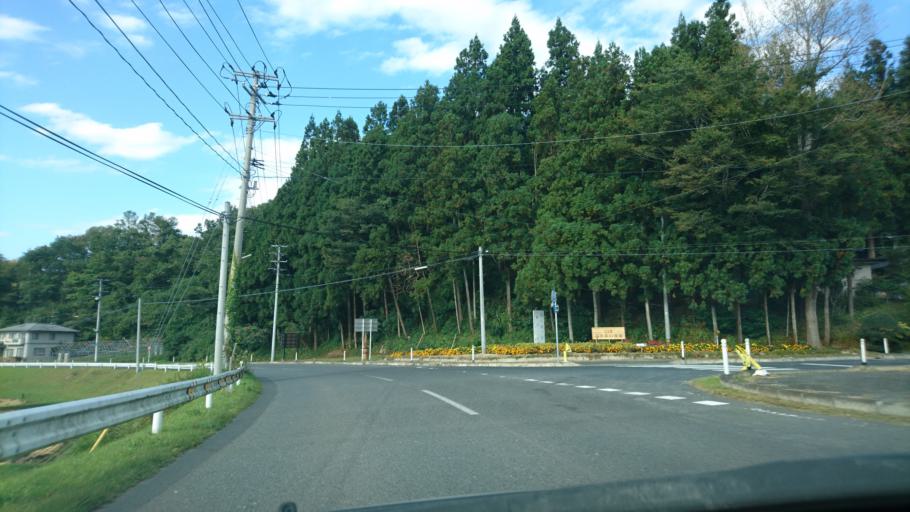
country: JP
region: Iwate
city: Ichinoseki
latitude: 38.8917
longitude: 141.3325
